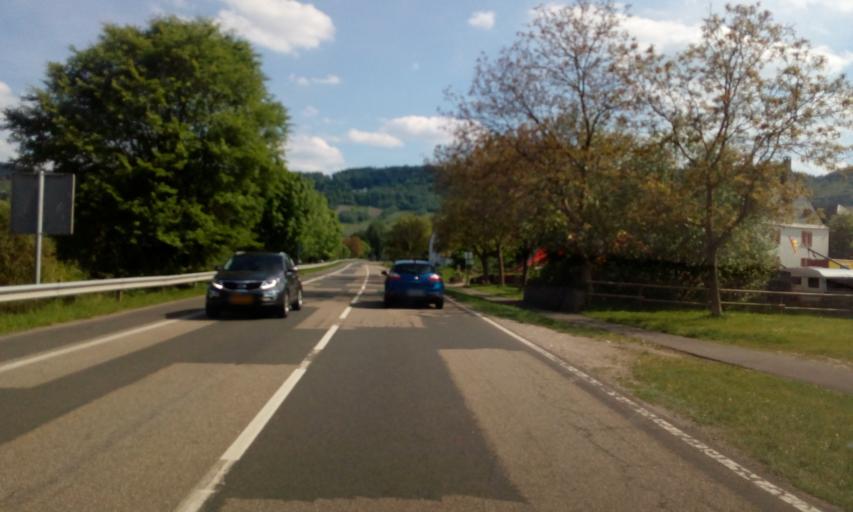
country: DE
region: Rheinland-Pfalz
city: Leiwen
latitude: 49.8244
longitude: 6.8824
